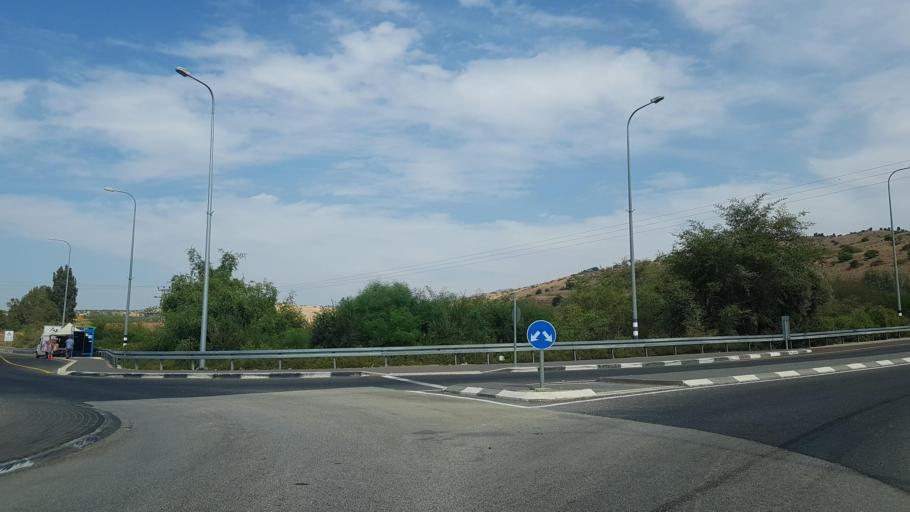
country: SY
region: Quneitra
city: Al Butayhah
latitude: 32.8825
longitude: 35.6603
